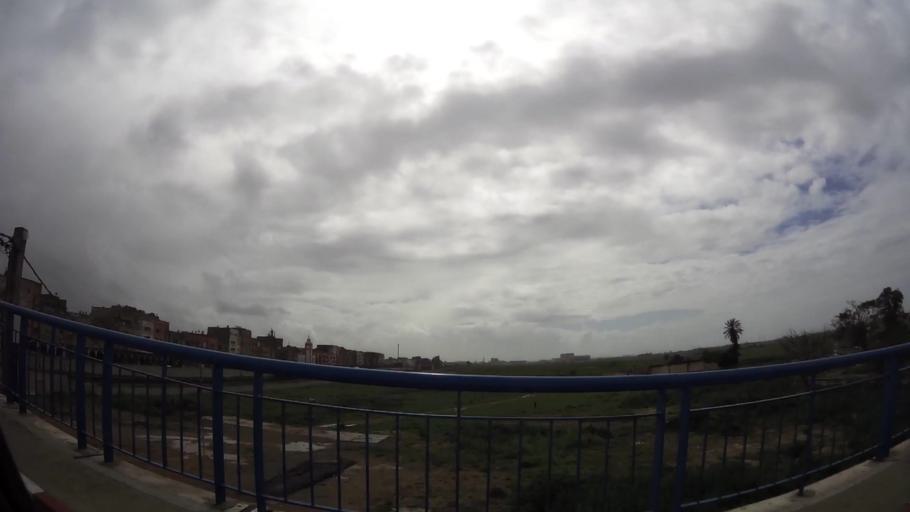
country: MA
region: Grand Casablanca
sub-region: Mohammedia
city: Mohammedia
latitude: 33.6416
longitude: -7.4509
